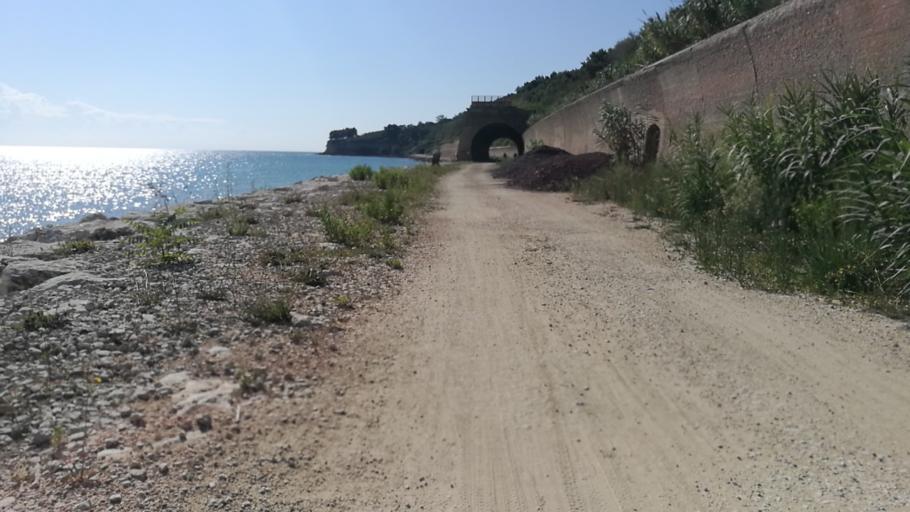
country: IT
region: Abruzzo
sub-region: Provincia di Chieti
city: Ortona
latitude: 42.3413
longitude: 14.4149
